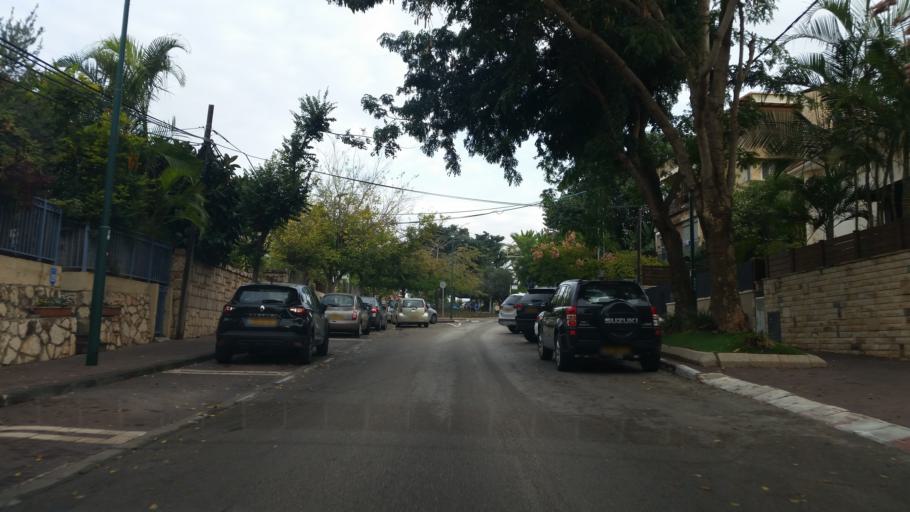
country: IL
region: Tel Aviv
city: Ramat HaSharon
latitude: 32.1587
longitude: 34.8498
